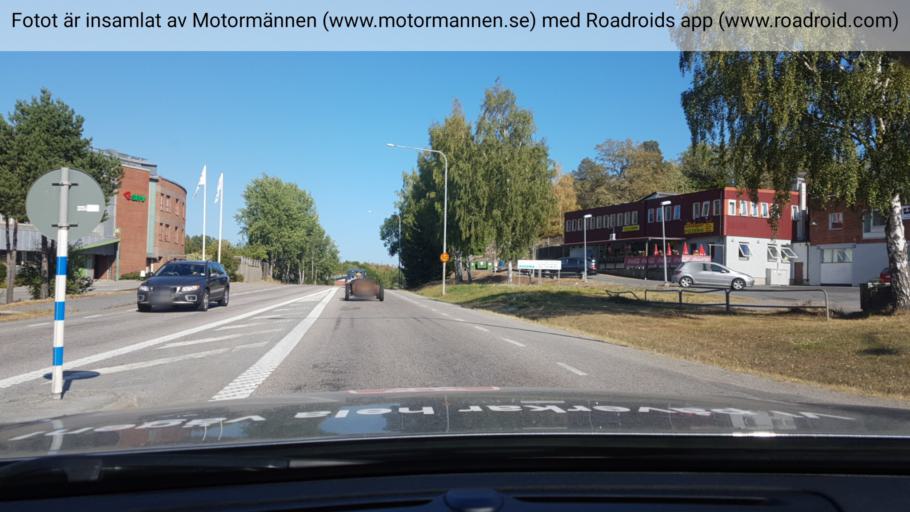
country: SE
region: Stockholm
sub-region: Huddinge Kommun
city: Huddinge
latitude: 59.2270
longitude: 17.9950
